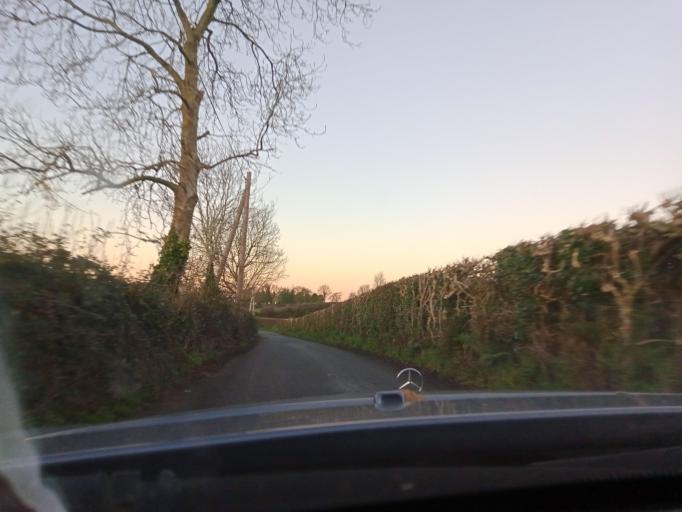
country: IE
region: Leinster
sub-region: Kilkenny
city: Thomastown
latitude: 52.4684
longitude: -7.0982
